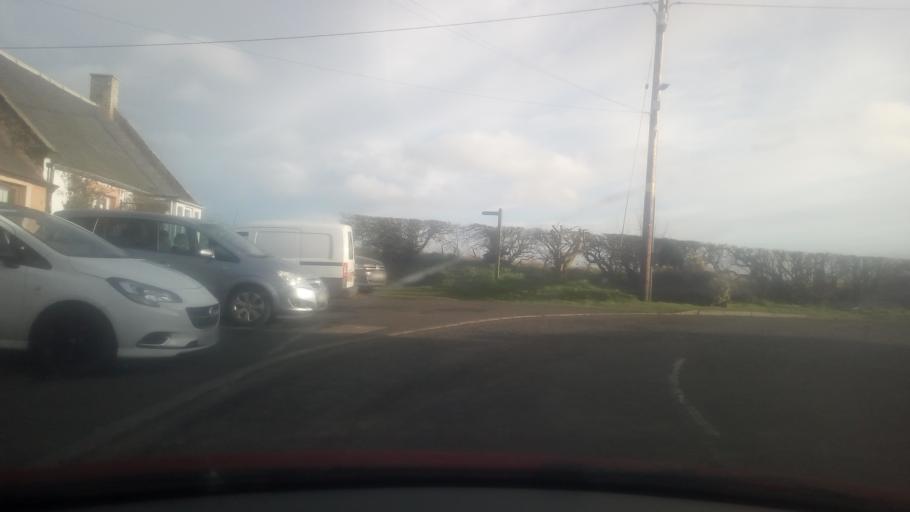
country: GB
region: Scotland
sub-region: The Scottish Borders
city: Coldstream
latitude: 55.7186
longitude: -2.2672
